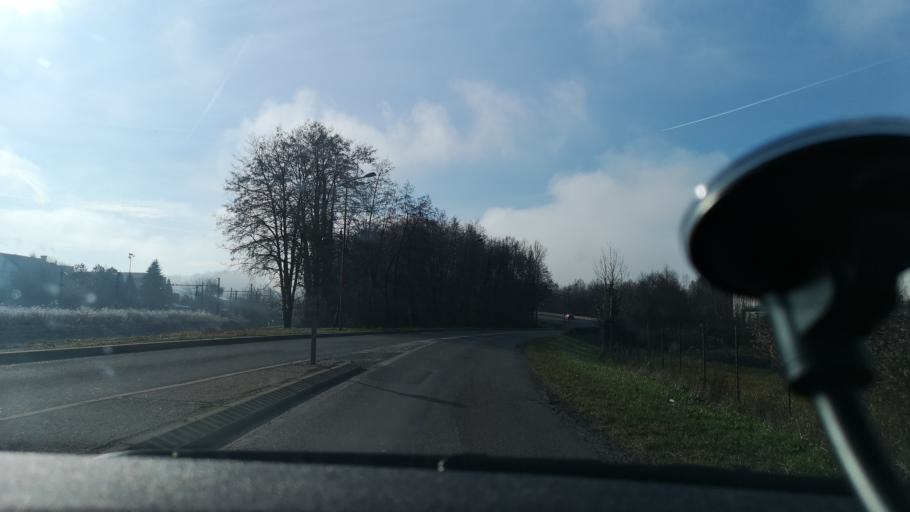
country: FR
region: Franche-Comte
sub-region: Departement du Doubs
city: Clerval
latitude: 47.4464
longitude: 6.5797
